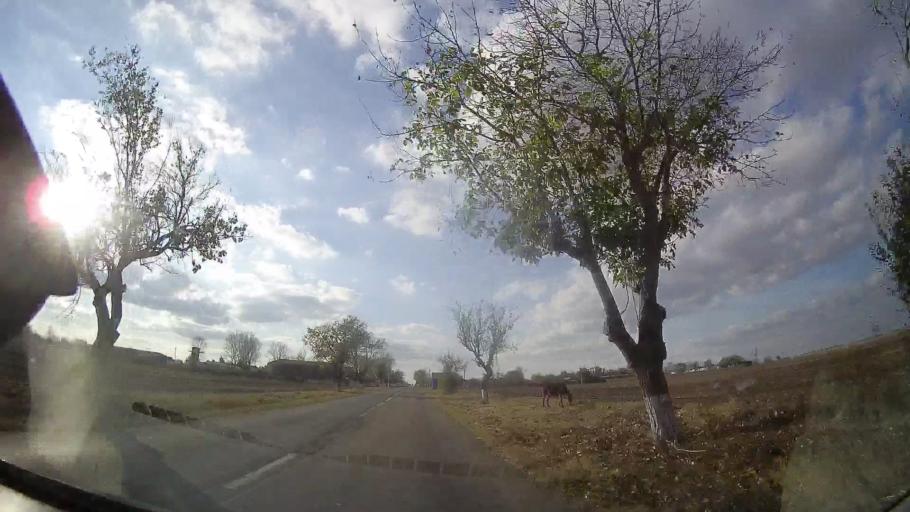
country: RO
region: Constanta
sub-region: Comuna Negru Voda
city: Negru Voda
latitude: 43.8194
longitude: 28.2316
